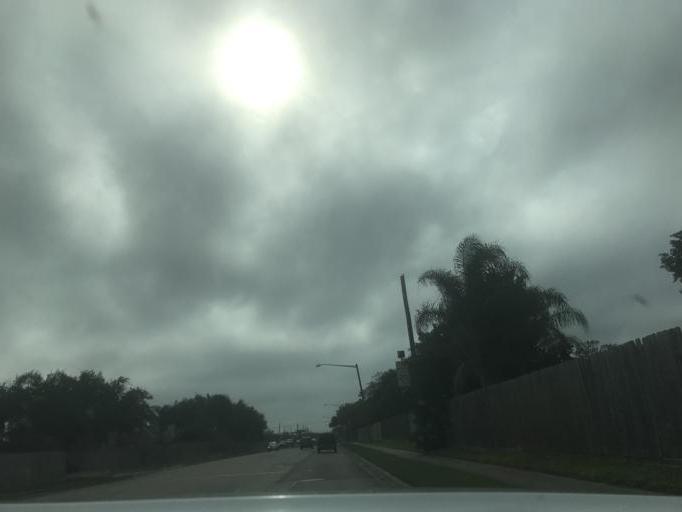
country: US
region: Texas
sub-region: Nueces County
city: Corpus Christi
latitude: 27.6832
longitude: -97.3668
